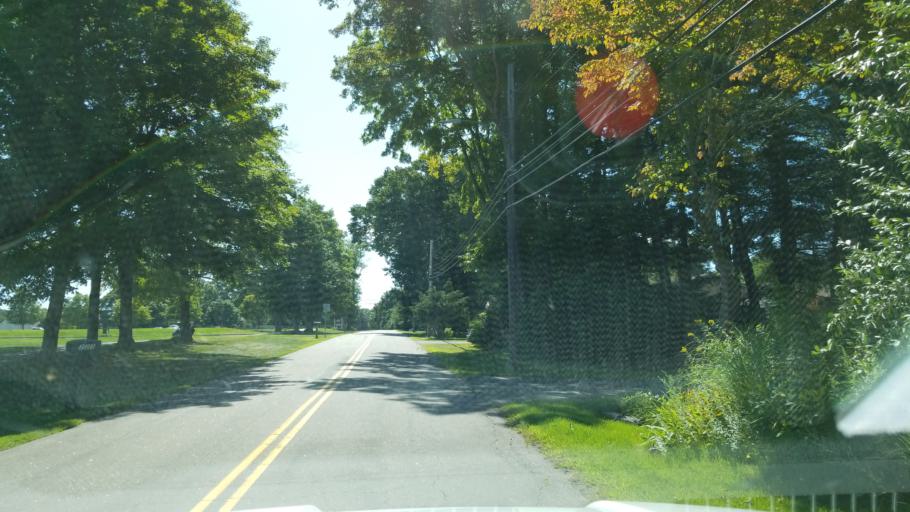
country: US
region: Connecticut
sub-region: Hartford County
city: Tariffville
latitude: 41.8584
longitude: -72.7604
